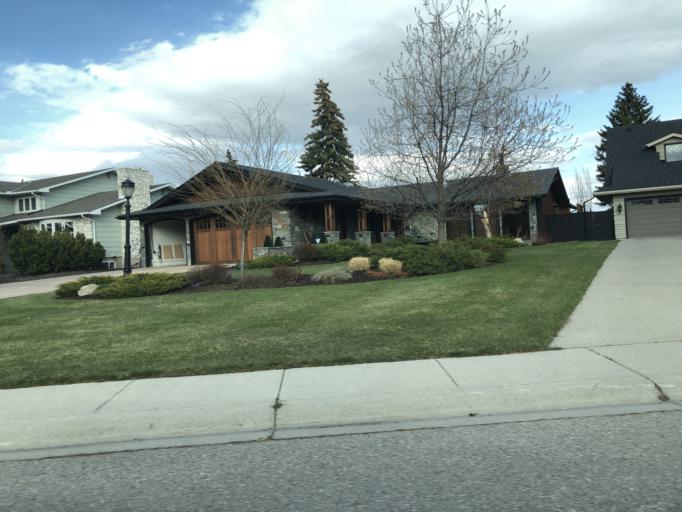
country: CA
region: Alberta
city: Calgary
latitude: 50.9446
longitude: -114.0543
